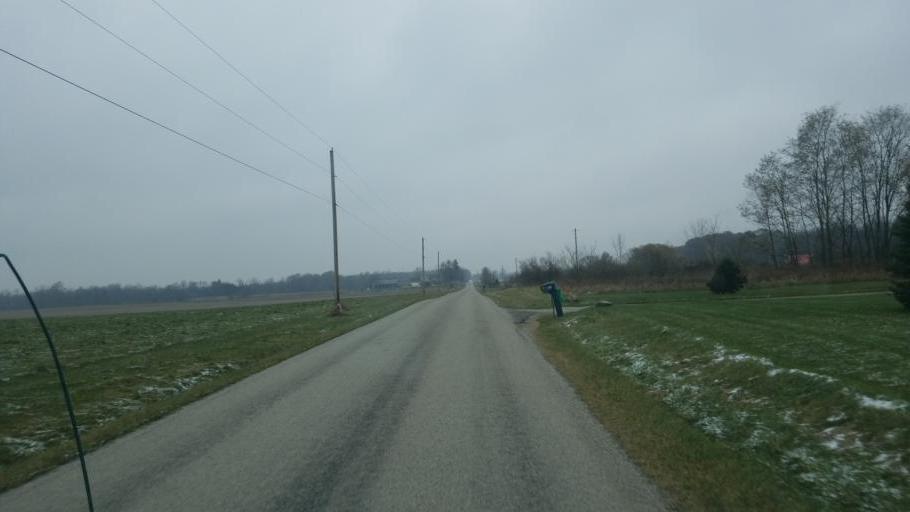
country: US
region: Ohio
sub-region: Huron County
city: New London
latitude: 41.0180
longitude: -82.3256
